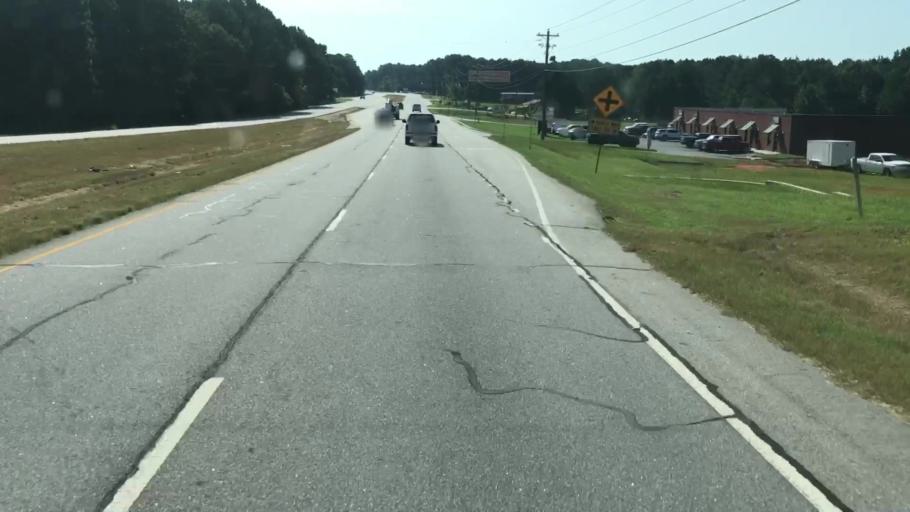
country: US
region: Georgia
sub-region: Walton County
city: Loganville
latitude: 33.8257
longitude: -83.8246
